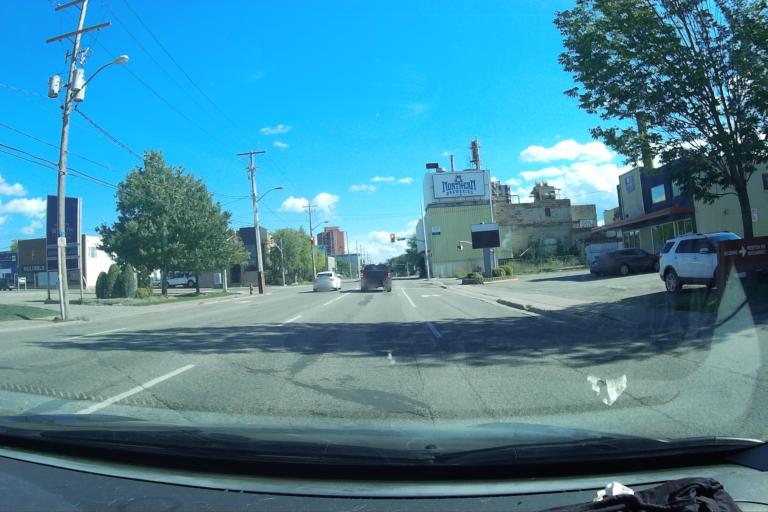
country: CA
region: Ontario
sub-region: Algoma
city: Sault Ste. Marie
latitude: 46.5097
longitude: -84.3331
